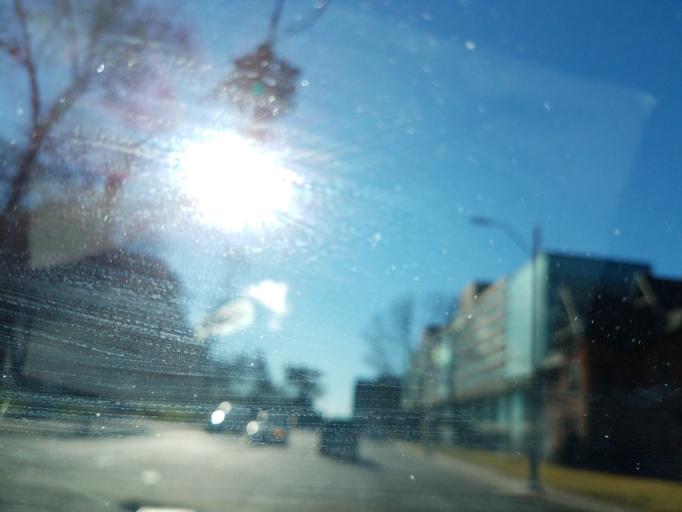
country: US
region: Connecticut
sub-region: Hartford County
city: Hartford
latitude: 41.7679
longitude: -72.6938
